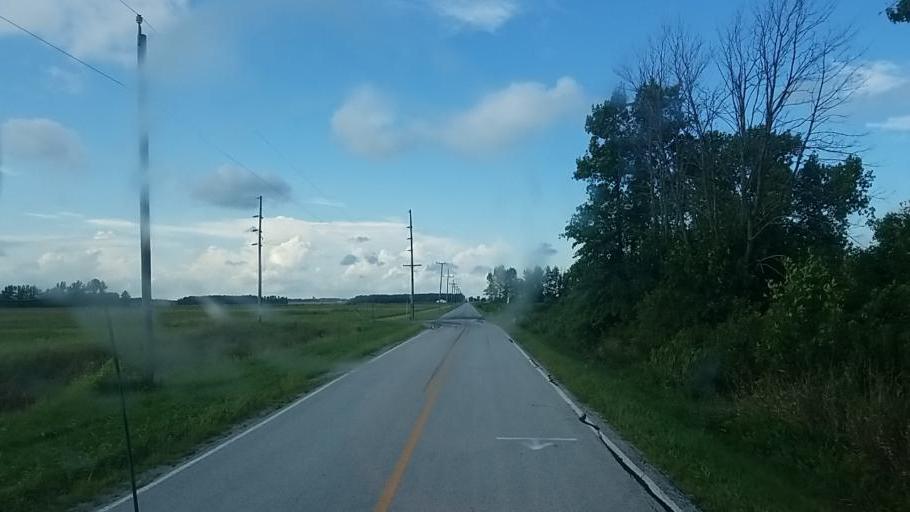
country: US
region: Ohio
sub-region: Hardin County
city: Forest
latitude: 40.7589
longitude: -83.4966
